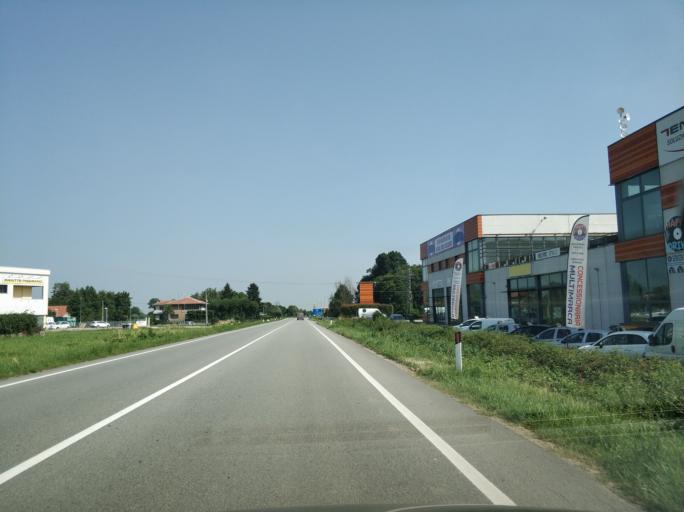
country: IT
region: Piedmont
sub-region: Provincia di Torino
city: Salassa
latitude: 45.3697
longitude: 7.6773
